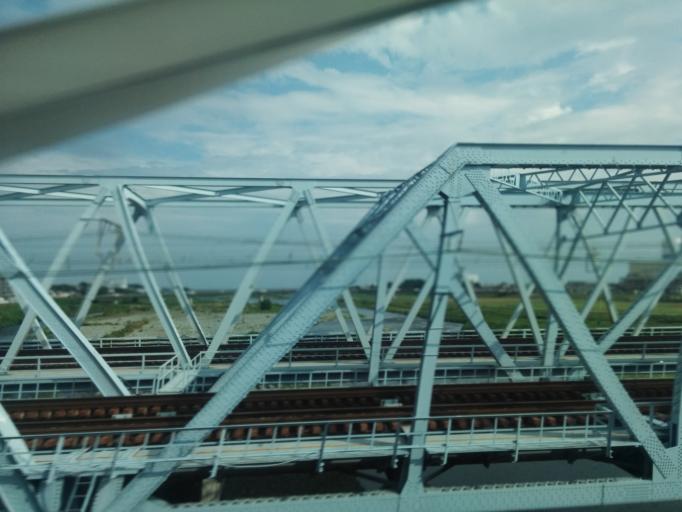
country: JP
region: Kanagawa
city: Odawara
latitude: 35.2717
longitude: 139.1704
